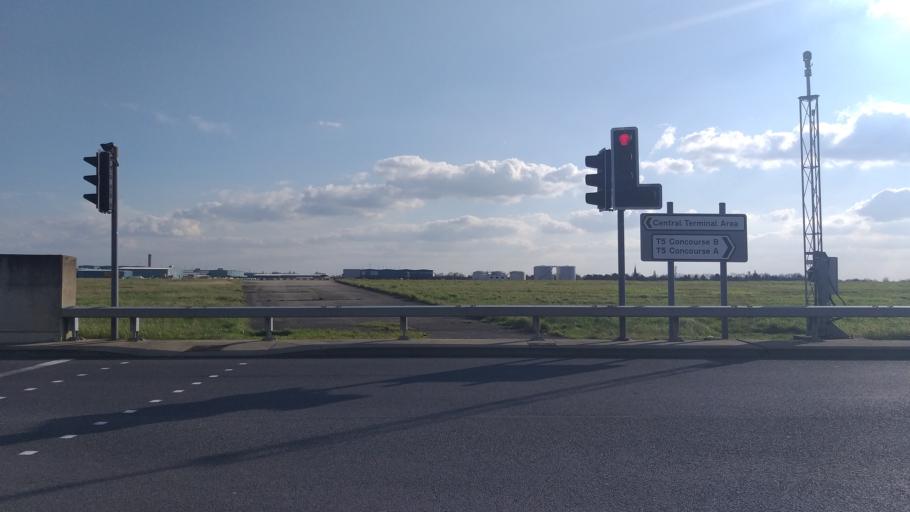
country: GB
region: England
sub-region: Greater London
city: West Drayton
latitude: 51.4681
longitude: -0.4760
